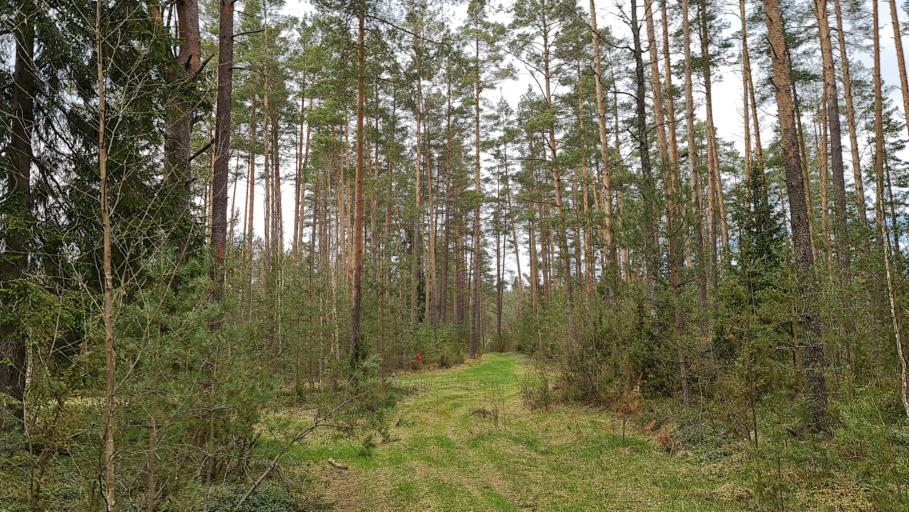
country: BY
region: Vitebsk
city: Byahoml'
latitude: 54.7380
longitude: 28.0324
